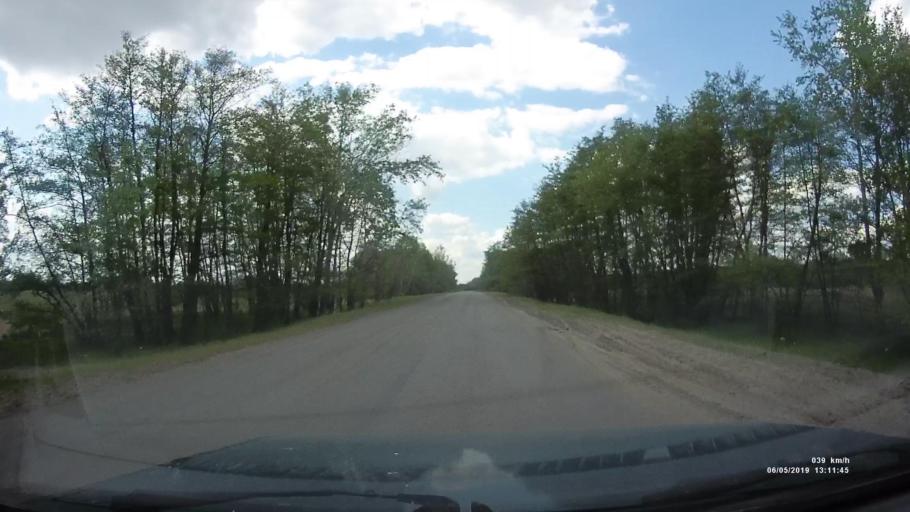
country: RU
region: Rostov
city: Ust'-Donetskiy
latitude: 47.7541
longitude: 40.9558
